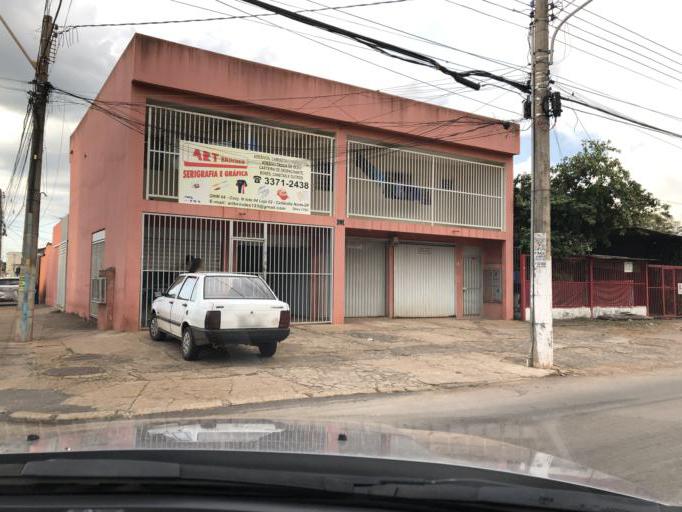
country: BR
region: Federal District
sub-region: Brasilia
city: Brasilia
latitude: -15.8126
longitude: -48.1081
